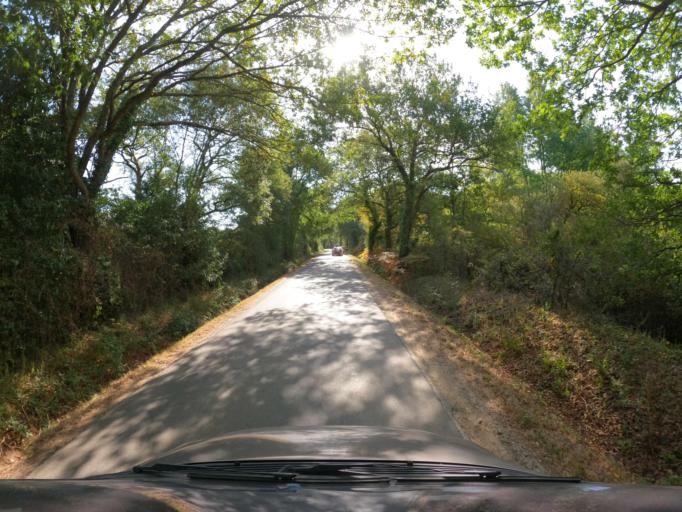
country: FR
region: Pays de la Loire
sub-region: Departement de la Vendee
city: Commequiers
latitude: 46.8130
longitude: -1.8212
